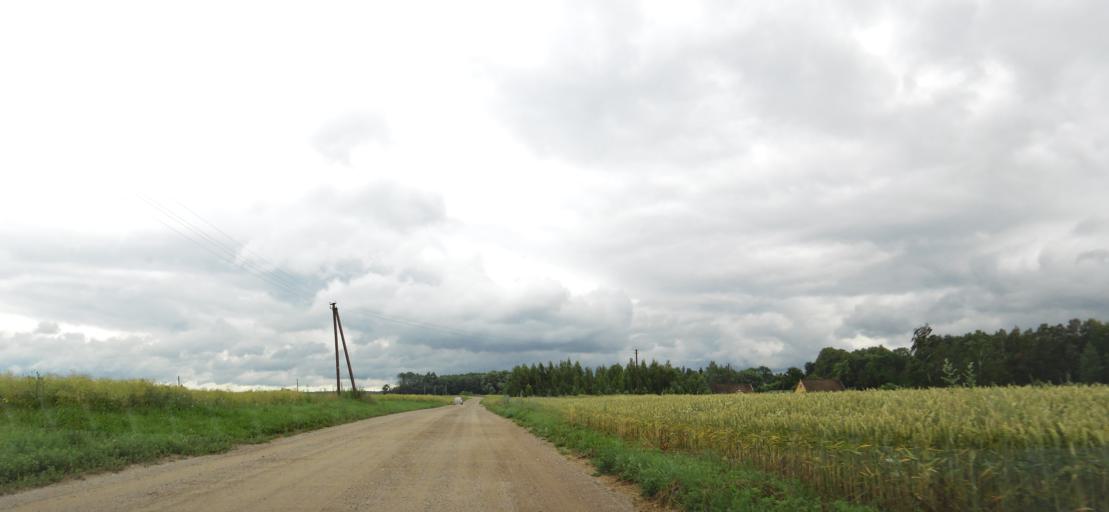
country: LT
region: Panevezys
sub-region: Birzai
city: Birzai
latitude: 56.1803
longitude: 24.7042
